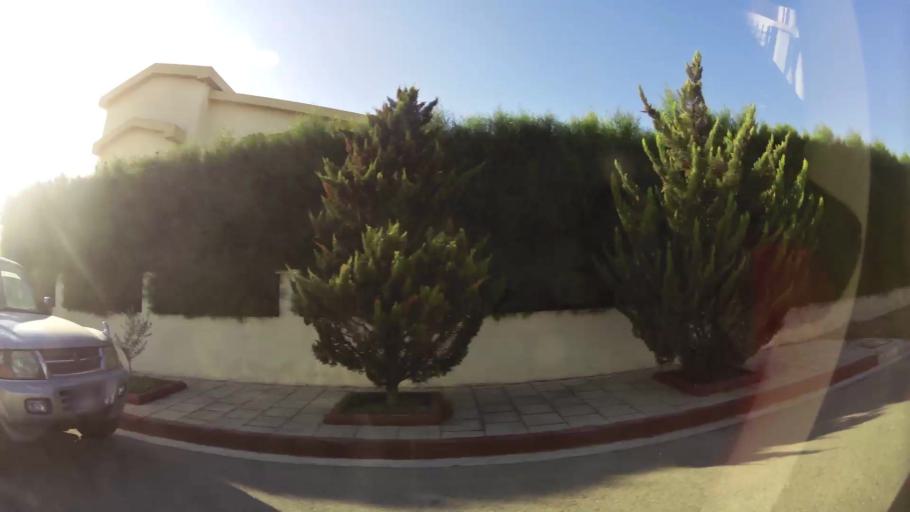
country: CY
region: Lefkosia
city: Nicosia
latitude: 35.2128
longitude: 33.2921
